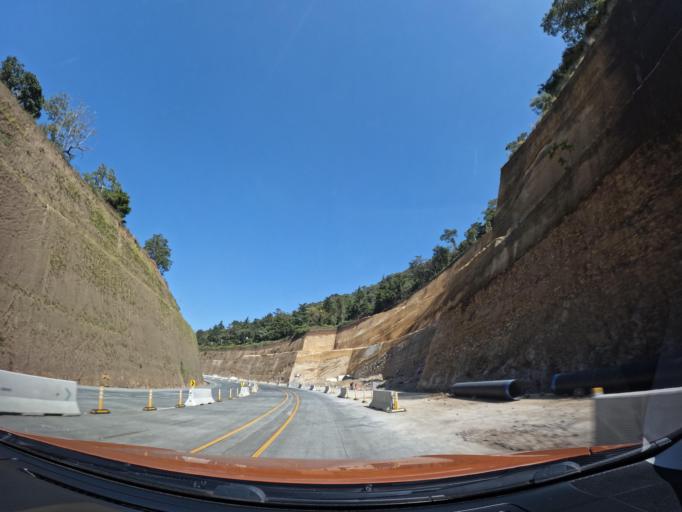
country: GT
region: Guatemala
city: Villa Canales
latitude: 14.4963
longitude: -90.5049
